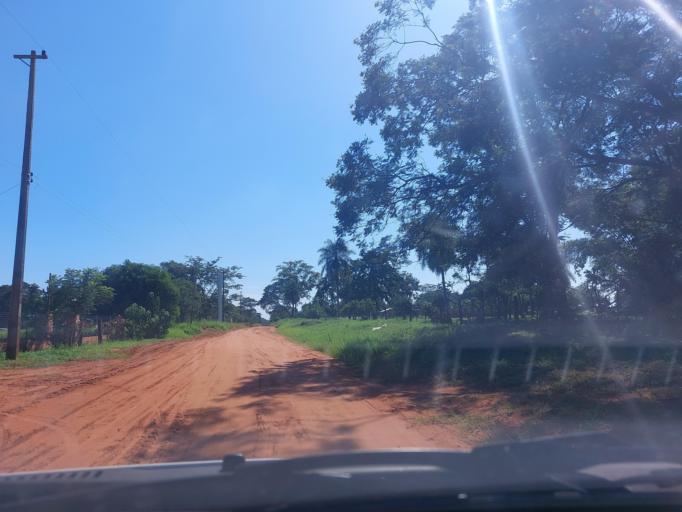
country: PY
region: San Pedro
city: Lima
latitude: -24.1544
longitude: -56.0114
